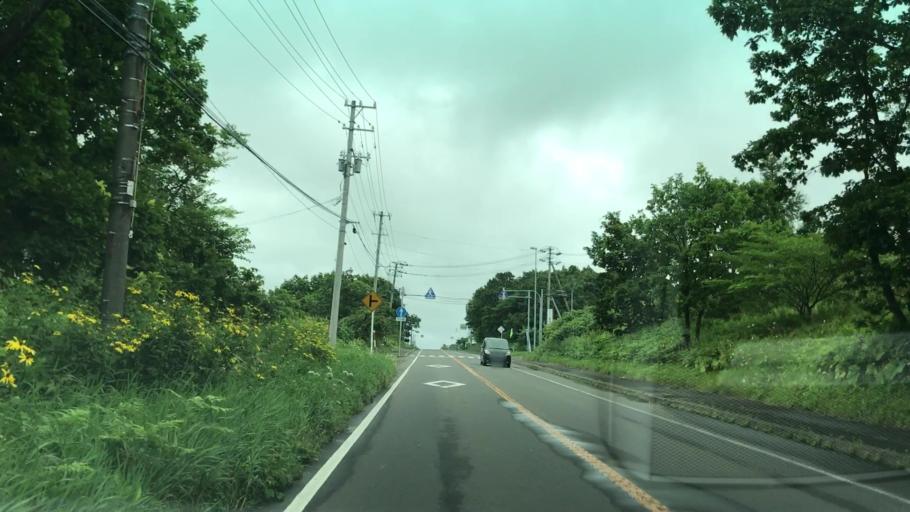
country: JP
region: Hokkaido
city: Muroran
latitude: 42.3802
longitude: 140.9742
